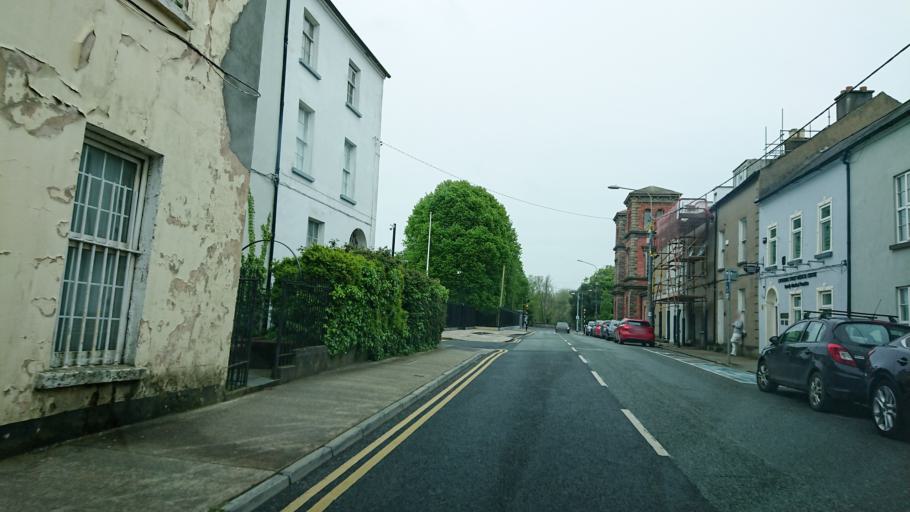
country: IE
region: Munster
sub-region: Waterford
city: Waterford
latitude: 52.2578
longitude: -7.1074
